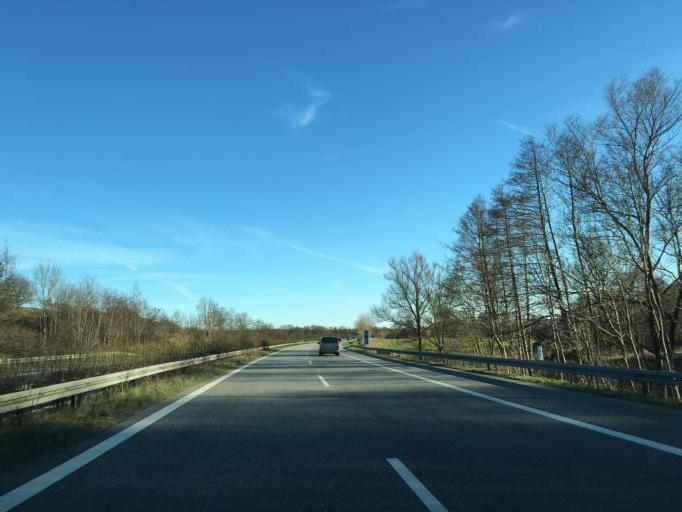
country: DE
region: Mecklenburg-Vorpommern
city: Lalendorf
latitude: 53.6920
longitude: 12.3685
